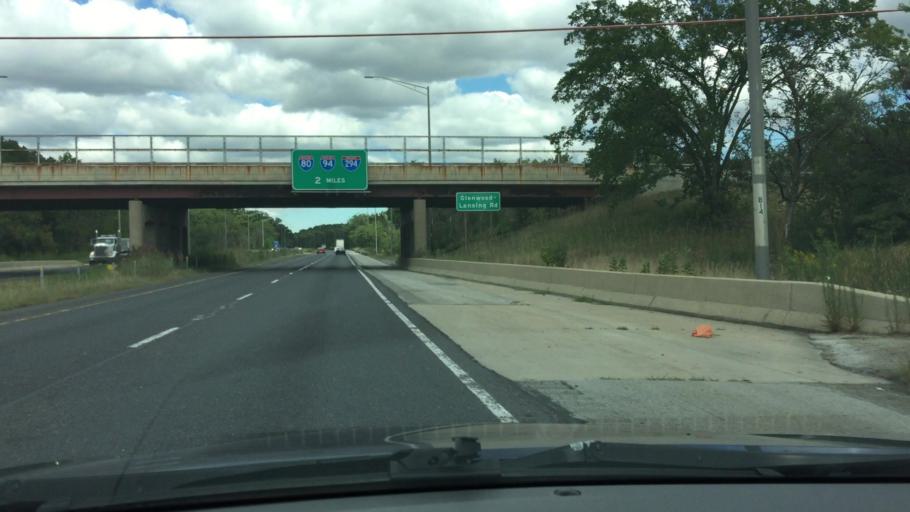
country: US
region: Illinois
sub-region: Cook County
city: Glenwood
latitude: 41.5421
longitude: -87.5824
